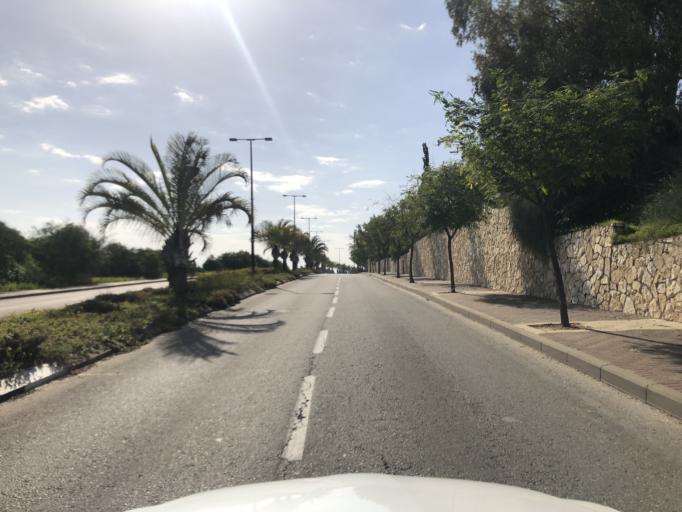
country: IL
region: Central District
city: Ness Ziona
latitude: 31.9169
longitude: 34.7935
